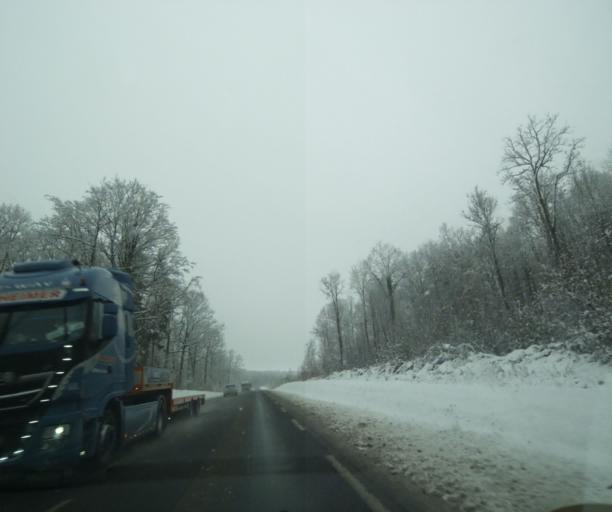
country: FR
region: Champagne-Ardenne
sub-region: Departement de la Haute-Marne
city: Laneuville-a-Remy
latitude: 48.5483
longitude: 4.8338
